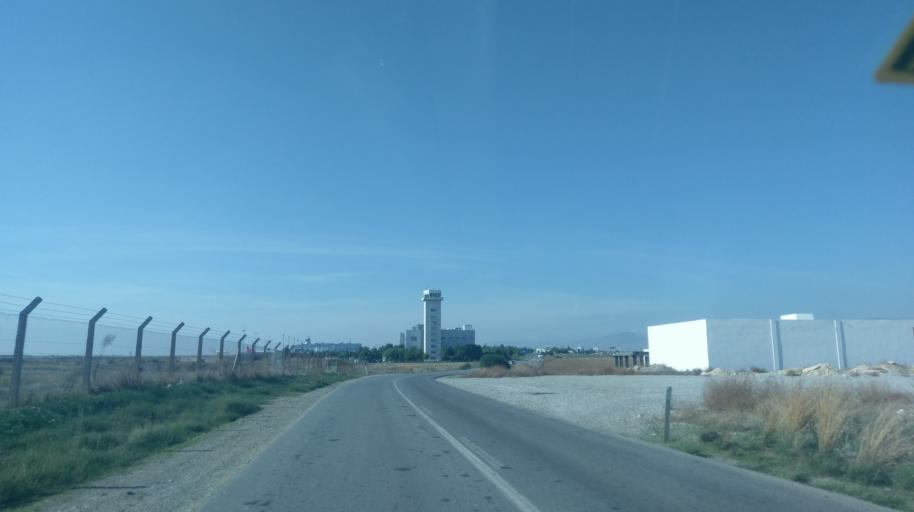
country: CY
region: Larnaka
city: Athienou
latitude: 35.1553
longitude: 33.5114
